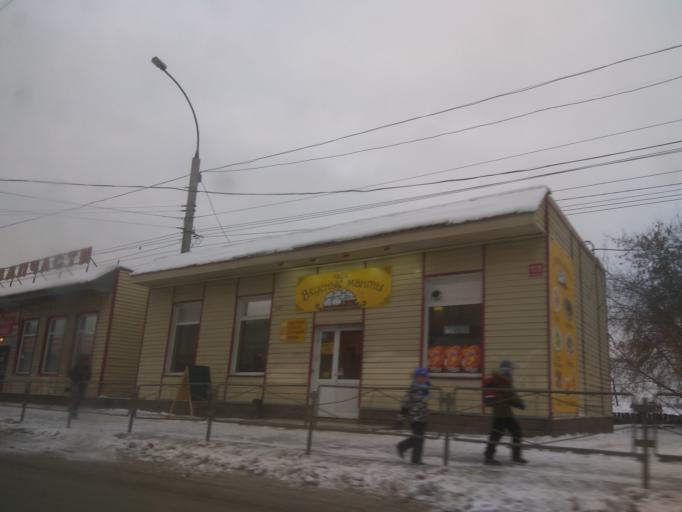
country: RU
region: Novosibirsk
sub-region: Novosibirskiy Rayon
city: Novosibirsk
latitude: 55.0305
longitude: 82.8933
